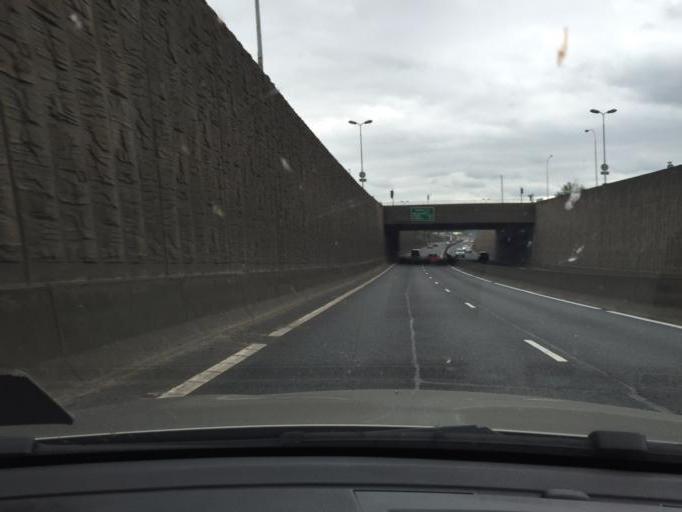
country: GB
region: Northern Ireland
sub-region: City of Belfast
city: Belfast
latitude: 54.6010
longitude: -5.9390
